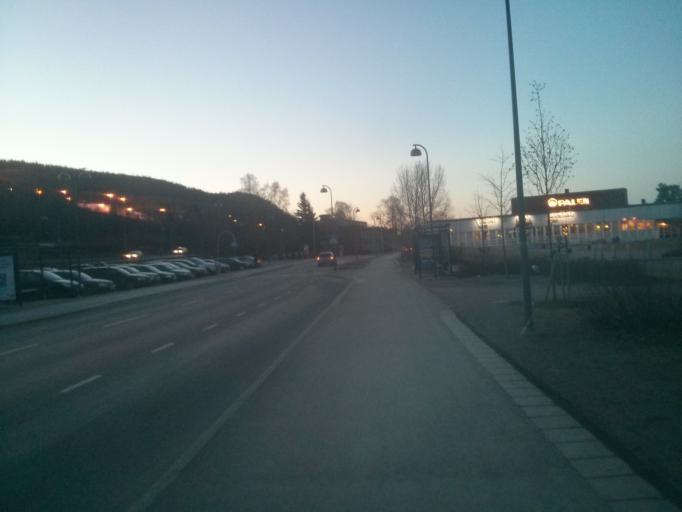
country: SE
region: Vaesternorrland
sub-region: Sundsvalls Kommun
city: Kvissleby
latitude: 62.2952
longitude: 17.3796
